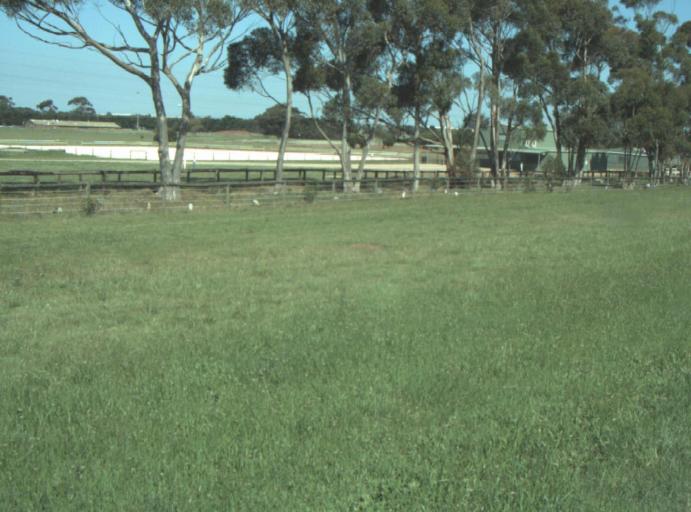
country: AU
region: Victoria
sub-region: Greater Geelong
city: Lara
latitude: -38.0305
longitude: 144.3546
